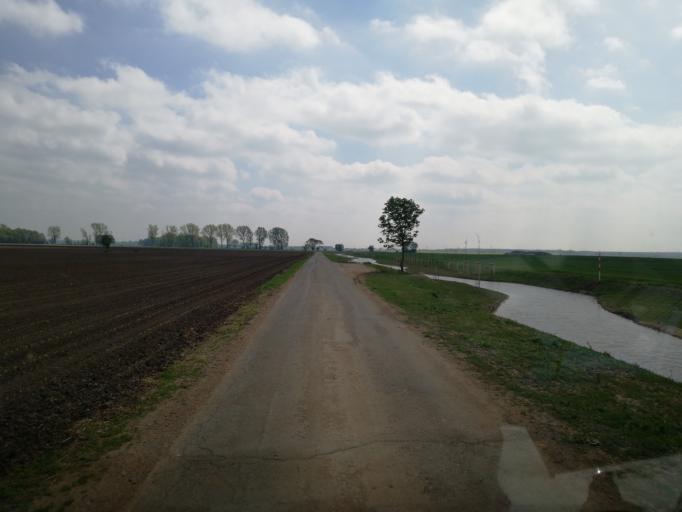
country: DE
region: Brandenburg
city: Doberlug-Kirchhain
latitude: 51.6819
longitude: 13.5346
